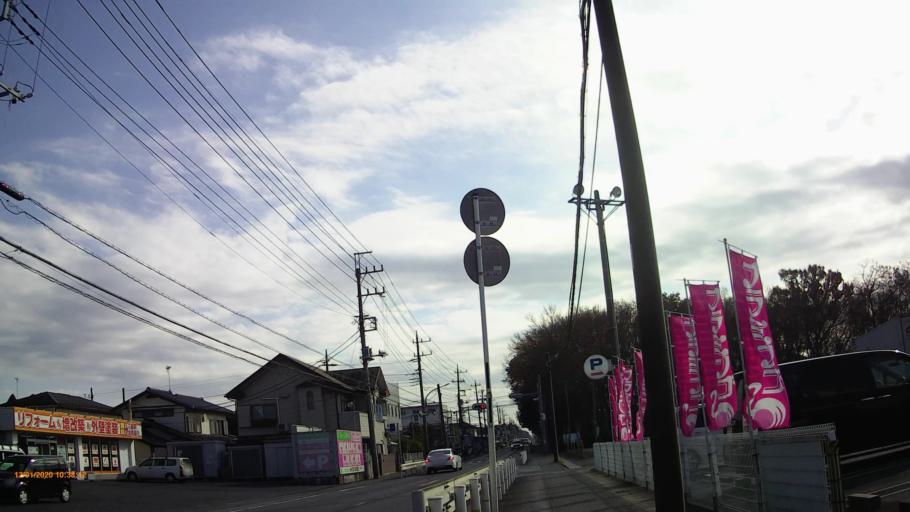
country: JP
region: Chiba
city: Yotsukaido
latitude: 35.6349
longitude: 140.1771
